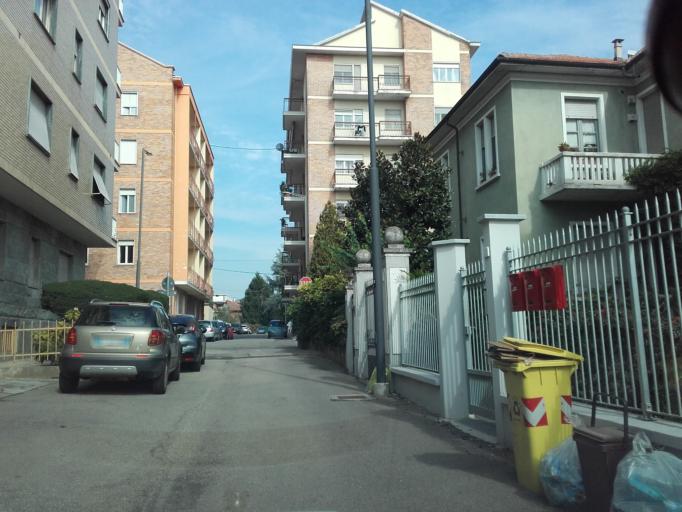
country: IT
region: Piedmont
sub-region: Provincia di Asti
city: Asti
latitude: 44.9051
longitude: 8.2062
